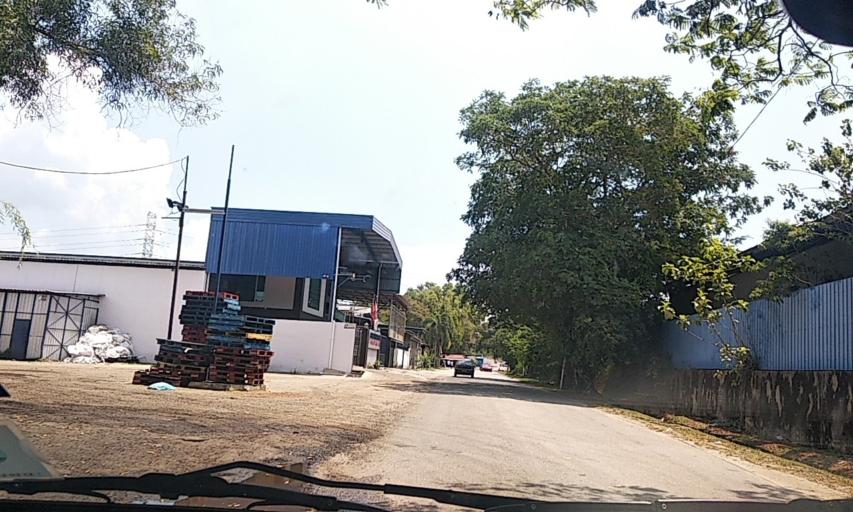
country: MY
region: Kedah
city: Sungai Petani
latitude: 5.6232
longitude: 100.4736
